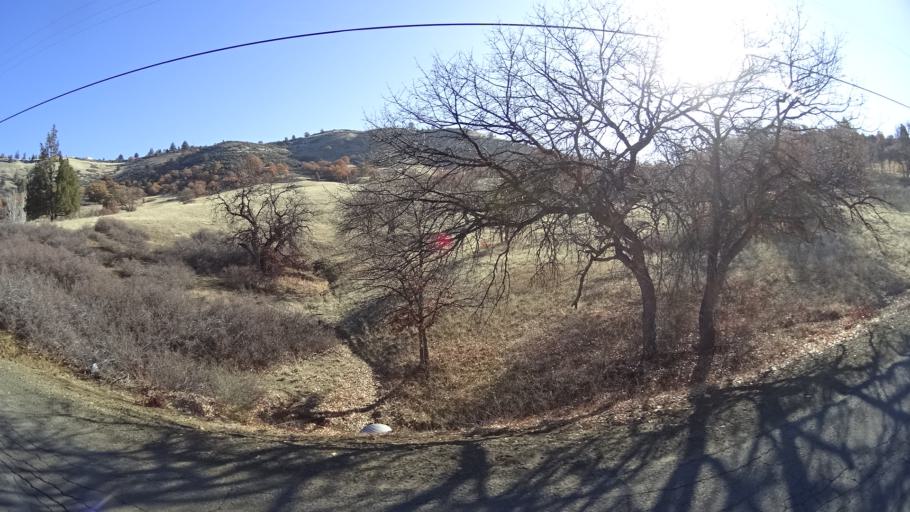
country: US
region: California
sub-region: Siskiyou County
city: Montague
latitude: 41.8822
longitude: -122.4729
